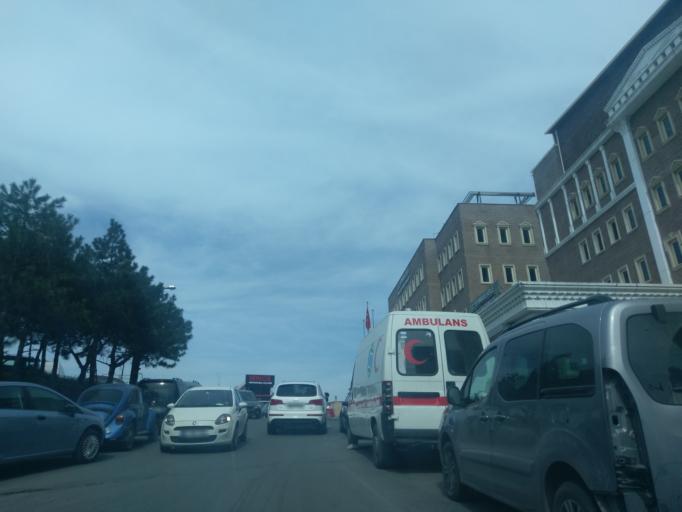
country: TR
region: Istanbul
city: Sisli
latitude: 41.1139
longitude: 29.0196
